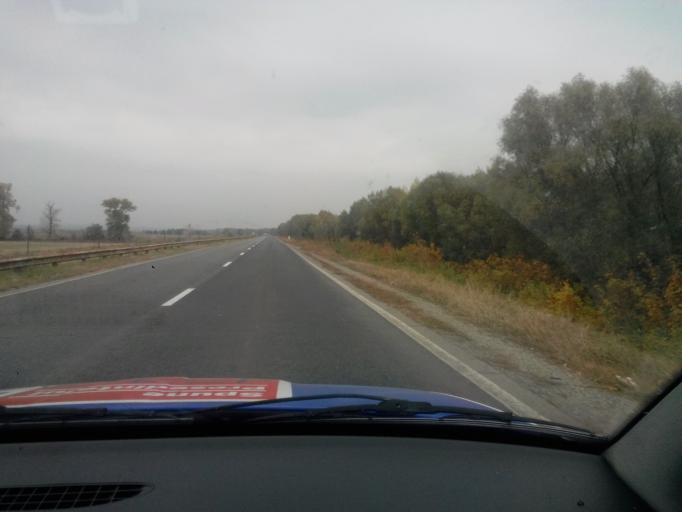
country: RO
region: Braila
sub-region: Municipiul Braila
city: Braila
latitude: 45.3306
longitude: 28.0001
